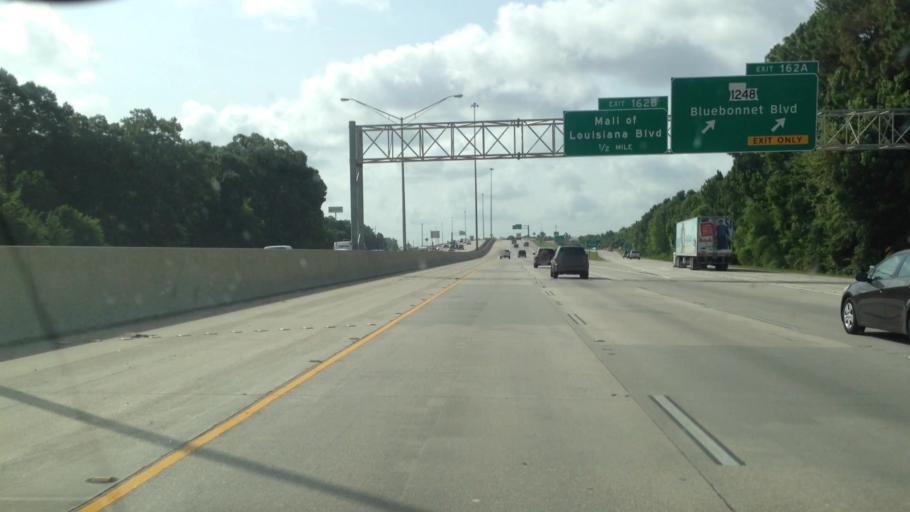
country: US
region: Louisiana
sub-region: East Baton Rouge Parish
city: Inniswold
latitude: 30.3991
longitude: -91.0909
